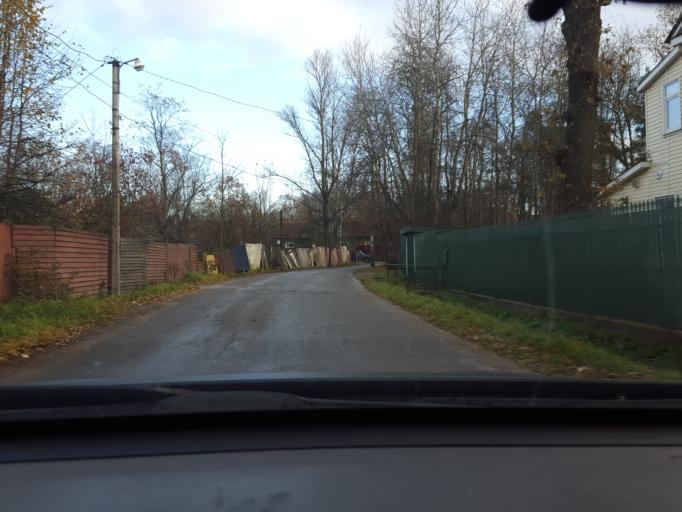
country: RU
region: St.-Petersburg
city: Shuvalovo
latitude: 60.0423
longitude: 30.2976
